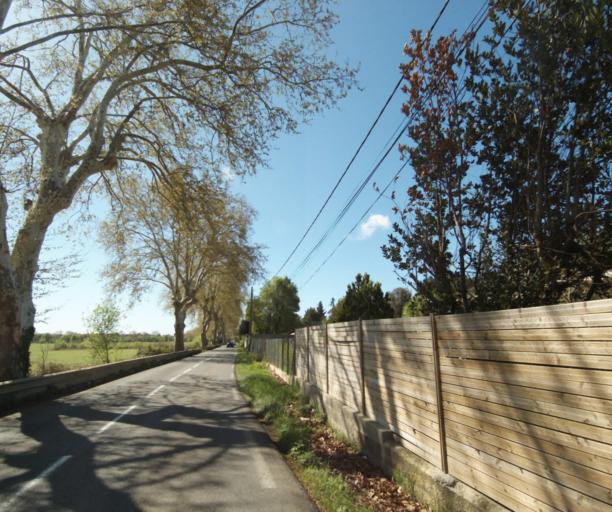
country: FR
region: Languedoc-Roussillon
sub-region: Departement de l'Herault
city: Villeneuve-les-Maguelone
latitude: 43.5520
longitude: 3.8464
